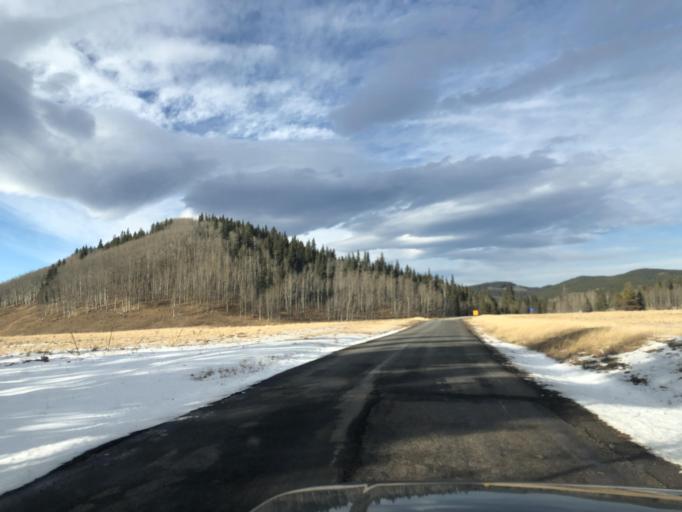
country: CA
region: Alberta
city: Cochrane
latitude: 51.0433
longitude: -114.8666
